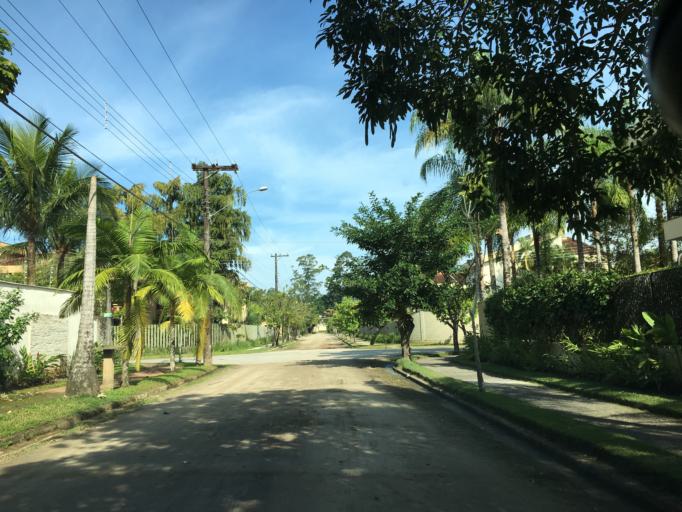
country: BR
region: Sao Paulo
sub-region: Sao Sebastiao
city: Sao Sebastiao
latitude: -23.7642
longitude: -45.7309
